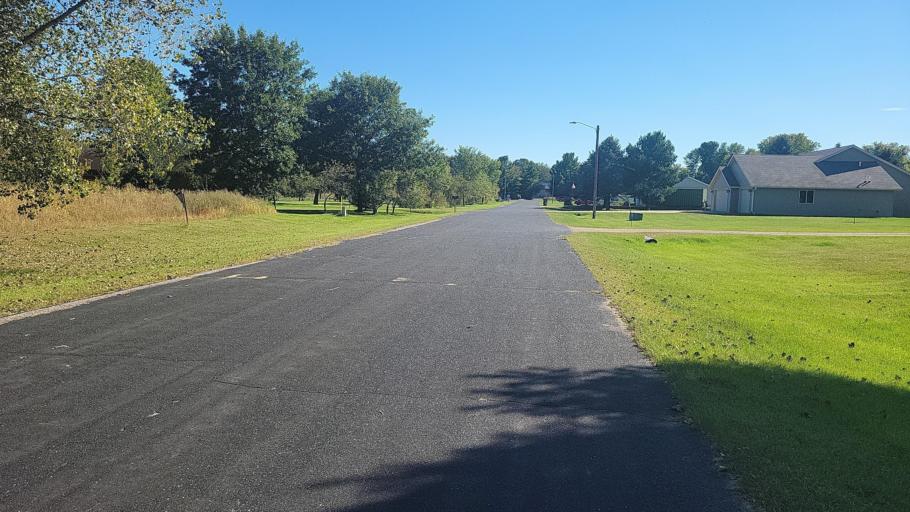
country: US
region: Wisconsin
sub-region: Dunn County
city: Menomonie
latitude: 44.7766
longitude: -91.9265
